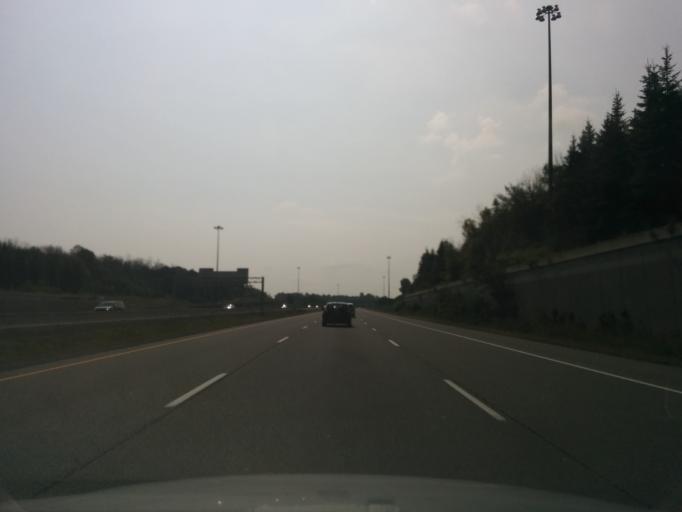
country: CA
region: Ontario
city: Bells Corners
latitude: 45.3312
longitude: -75.8094
